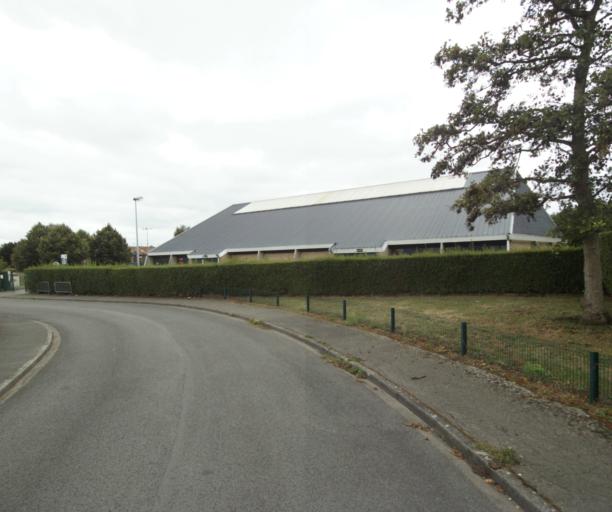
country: FR
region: Nord-Pas-de-Calais
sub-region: Departement du Nord
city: Leers
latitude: 50.6781
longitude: 3.2426
